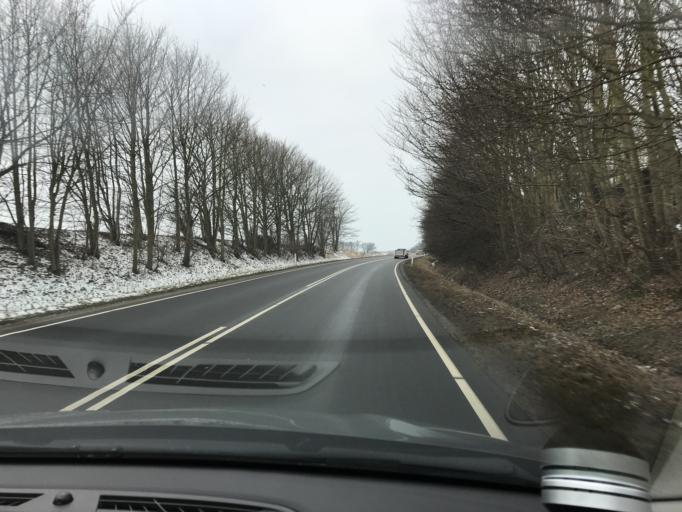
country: DK
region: Zealand
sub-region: Odsherred Kommune
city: Horve
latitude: 55.7808
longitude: 11.3996
